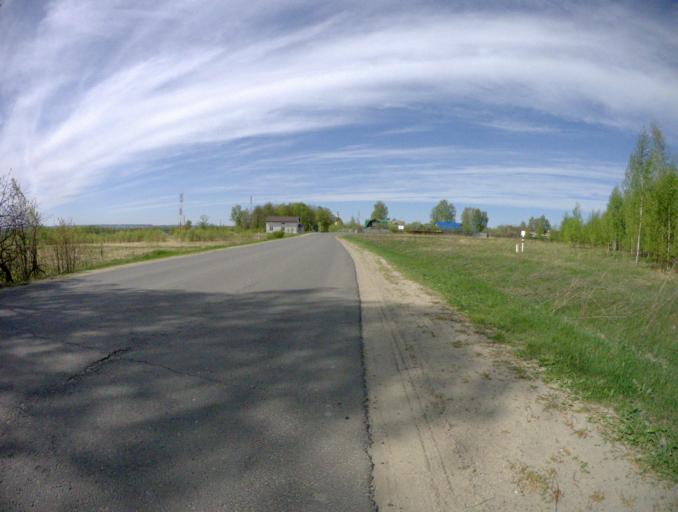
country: RU
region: Vladimir
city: Orgtrud
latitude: 56.2038
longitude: 40.5867
